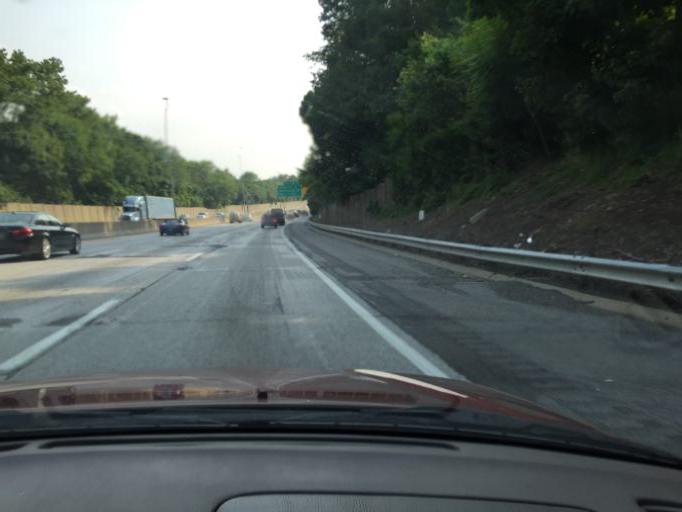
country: US
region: New York
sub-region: Westchester County
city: Harrison
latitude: 40.9655
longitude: -73.7289
